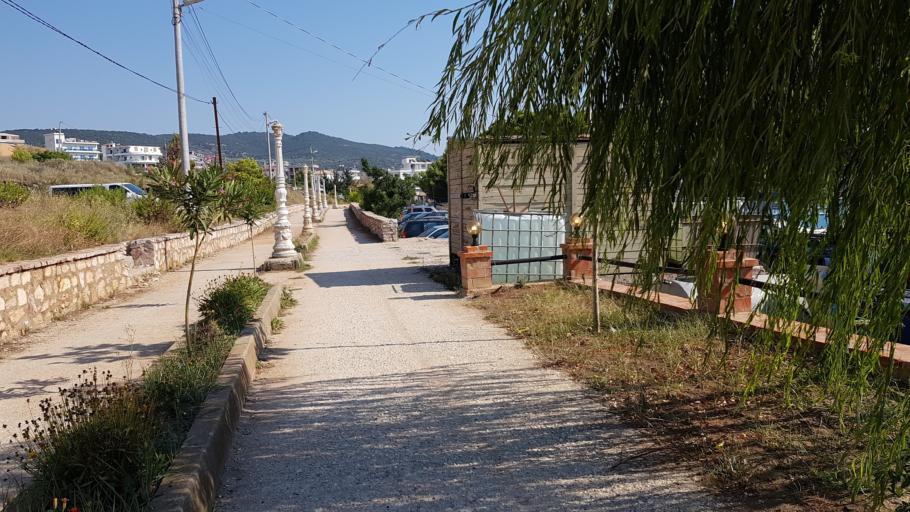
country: AL
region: Vlore
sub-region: Rrethi i Sarandes
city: Xarre
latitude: 39.7751
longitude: 20.0018
